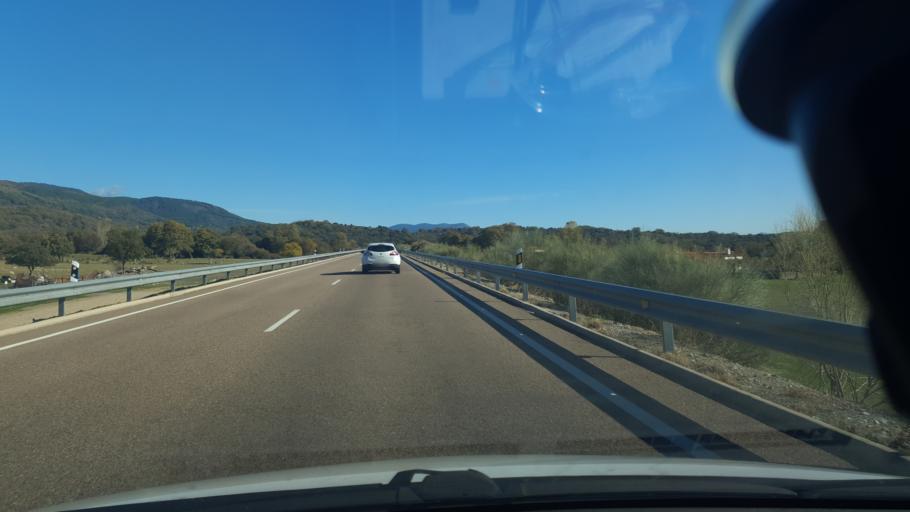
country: ES
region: Castille and Leon
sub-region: Provincia de Avila
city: Poyales del Hoyo
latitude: 40.1442
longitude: -5.1976
